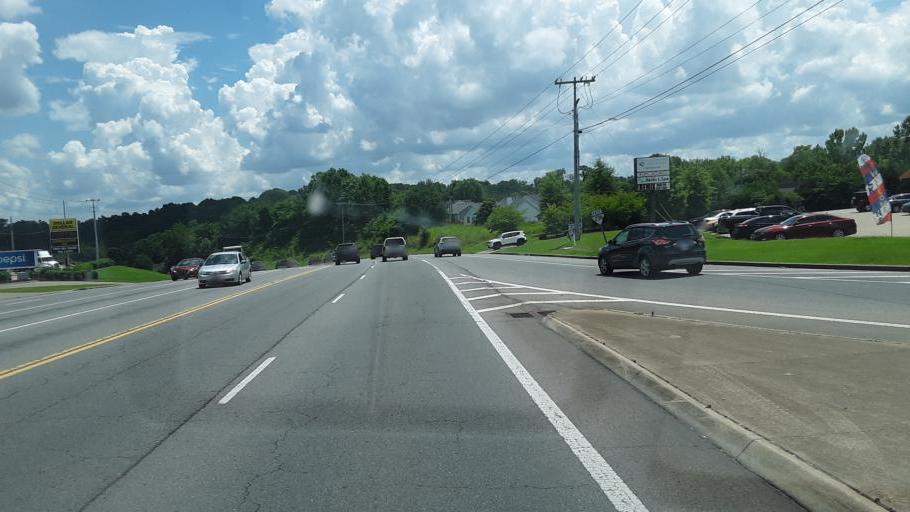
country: US
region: Kentucky
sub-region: Christian County
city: Oak Grove
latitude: 36.6252
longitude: -87.3699
